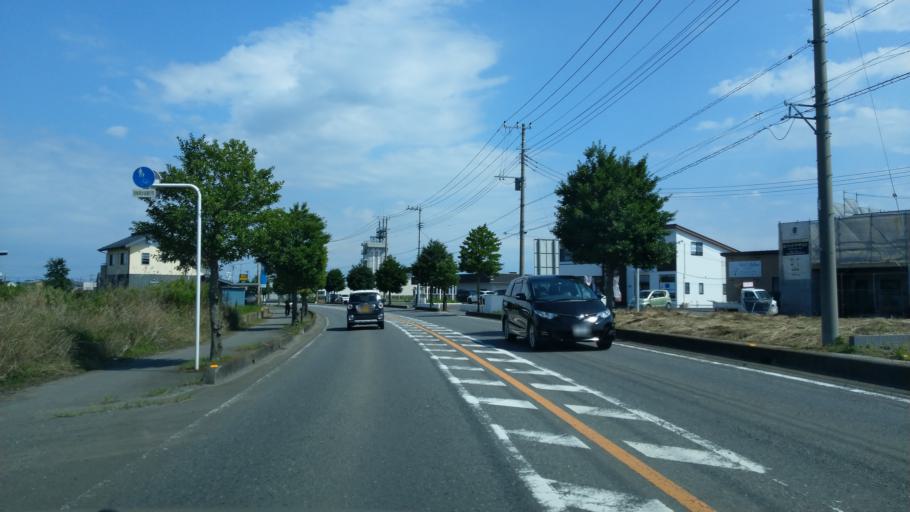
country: JP
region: Saitama
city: Honjo
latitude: 36.2352
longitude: 139.1620
